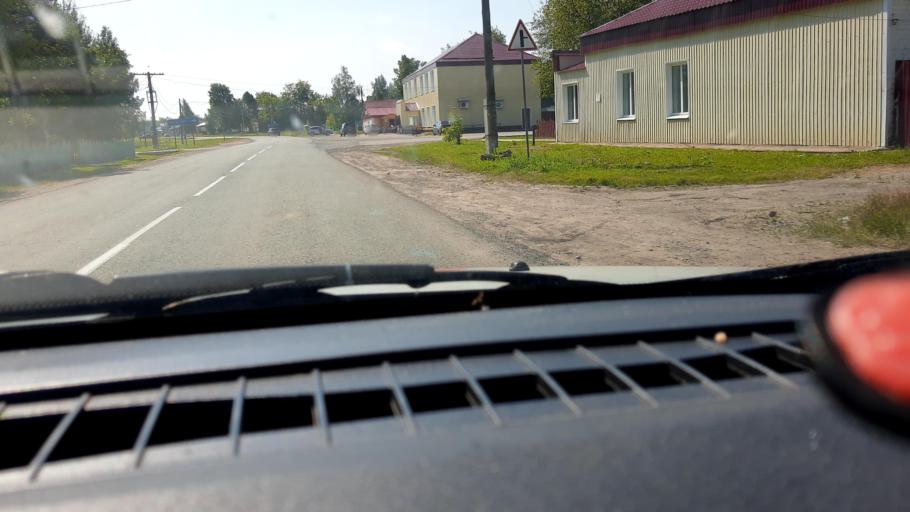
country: RU
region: Nizjnij Novgorod
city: Sharanga
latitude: 57.0517
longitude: 46.5454
